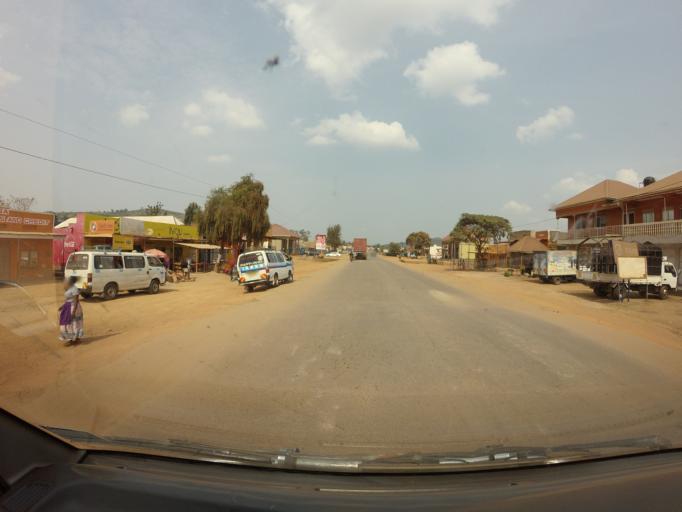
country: UG
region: Central Region
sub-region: Lwengo District
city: Lwengo
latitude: -0.3886
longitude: 31.3213
